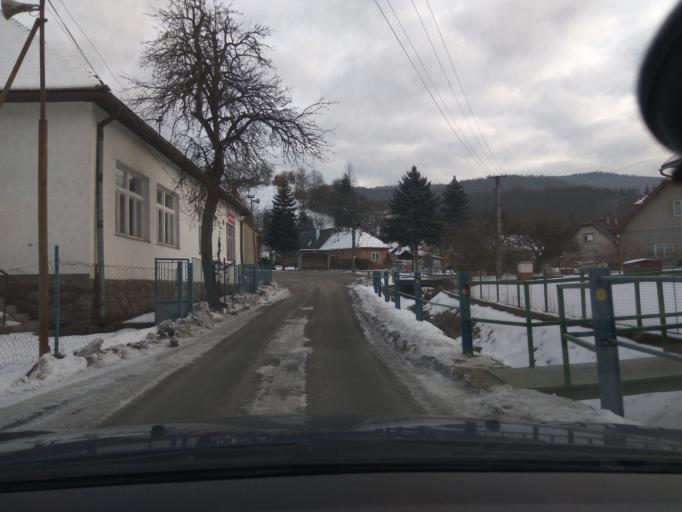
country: SK
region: Banskobystricky
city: Zarnovica
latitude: 48.4810
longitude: 18.7526
